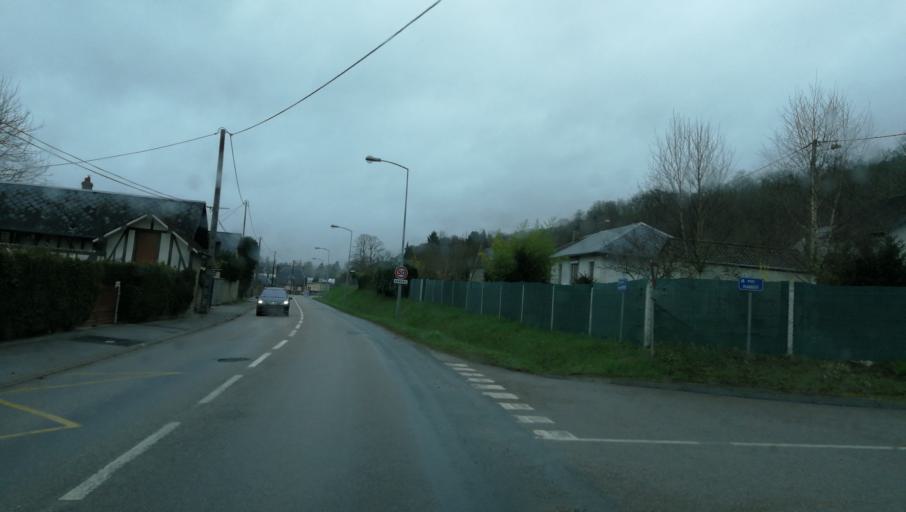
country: FR
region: Haute-Normandie
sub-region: Departement de l'Eure
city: Brionne
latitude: 49.1803
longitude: 0.7258
